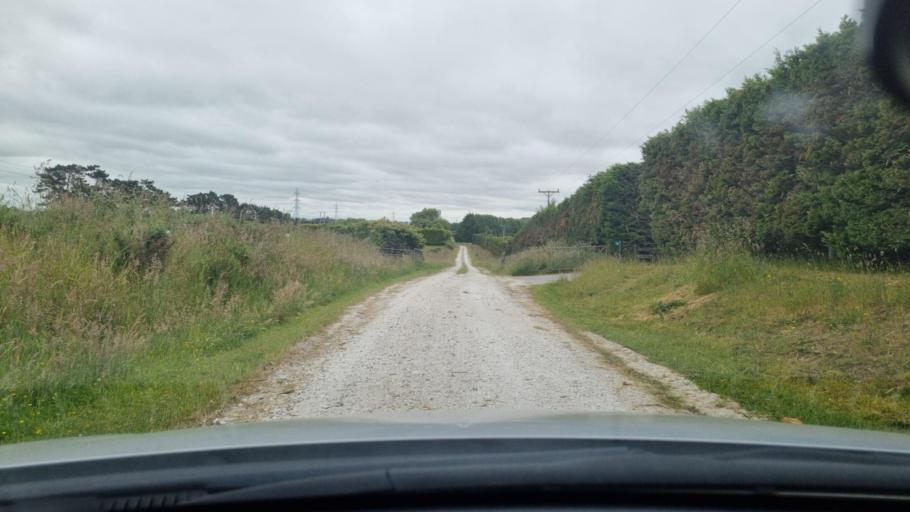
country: NZ
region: Southland
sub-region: Invercargill City
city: Invercargill
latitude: -46.3914
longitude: 168.4053
